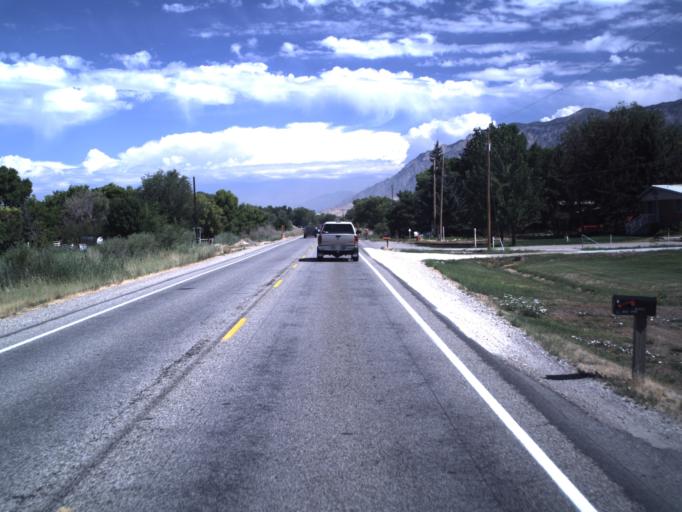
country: US
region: Utah
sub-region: Weber County
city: Marriott-Slaterville
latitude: 41.2538
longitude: -112.0252
